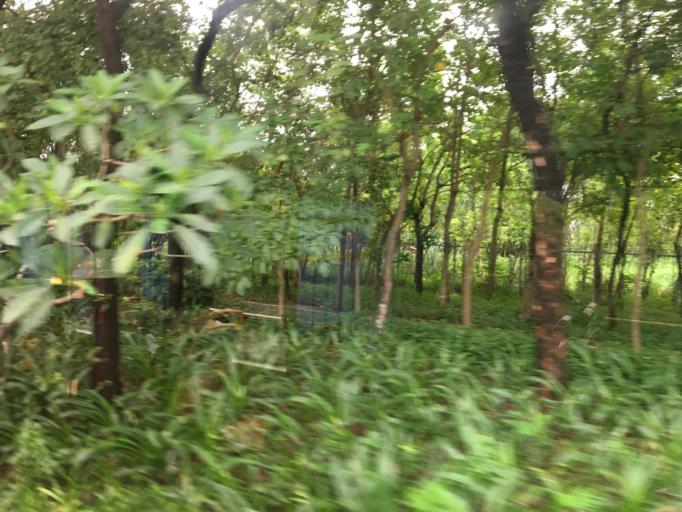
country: CN
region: Guangdong
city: Shahe
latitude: 22.5313
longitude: 113.9694
